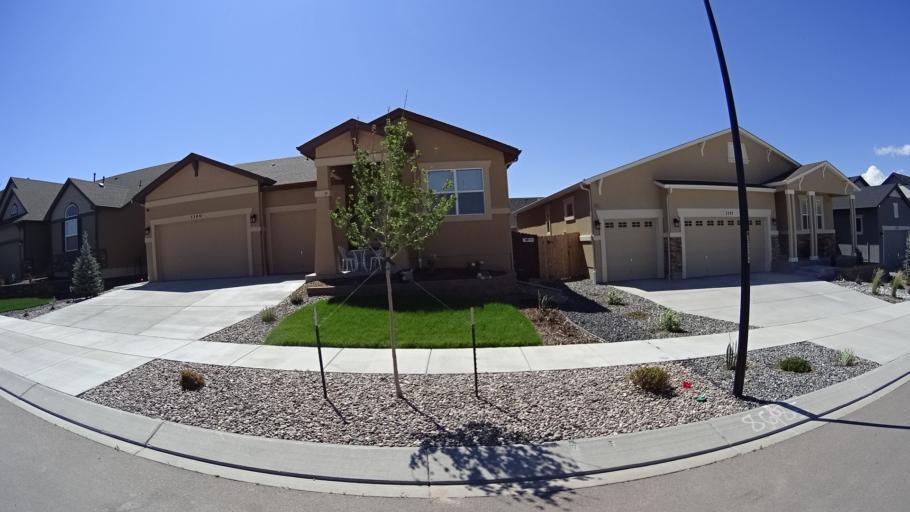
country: US
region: Colorado
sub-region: El Paso County
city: Black Forest
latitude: 38.9933
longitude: -104.7652
